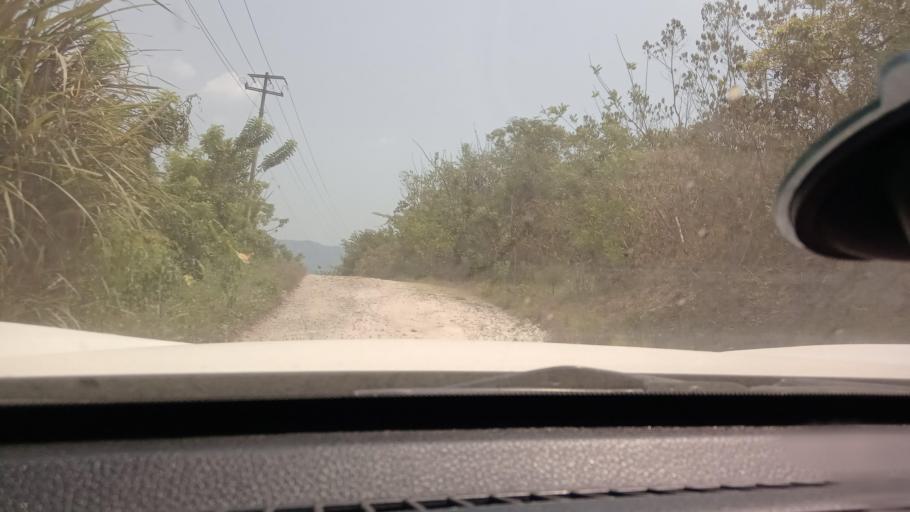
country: MX
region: Tabasco
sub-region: Huimanguillo
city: Francisco Rueda
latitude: 17.4779
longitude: -93.9464
